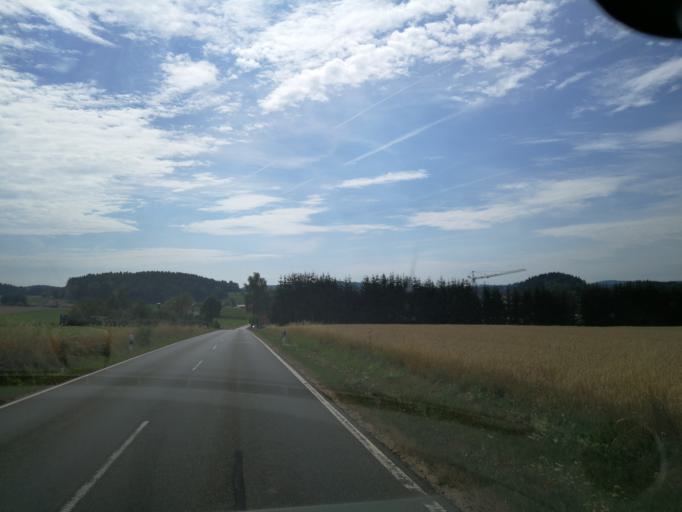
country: DE
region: Bavaria
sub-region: Upper Palatinate
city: Falkenstein
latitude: 49.0721
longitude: 12.5136
